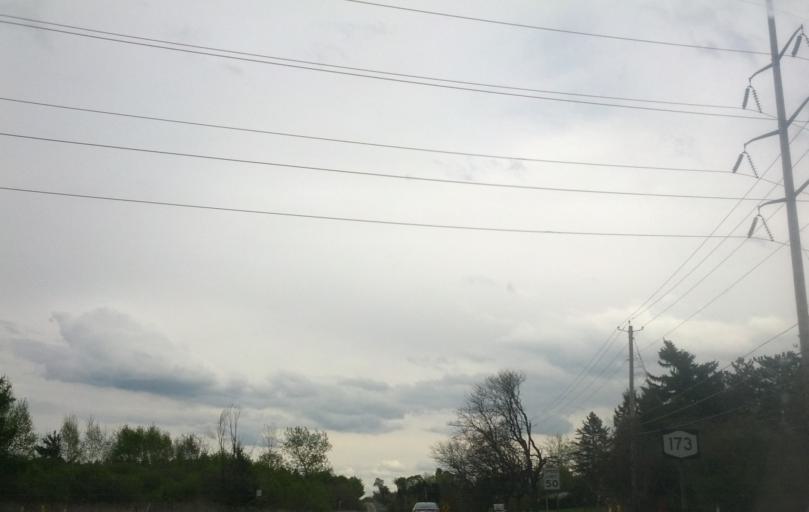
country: US
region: New York
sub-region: Onondaga County
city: Nedrow
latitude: 42.9988
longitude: -76.1229
